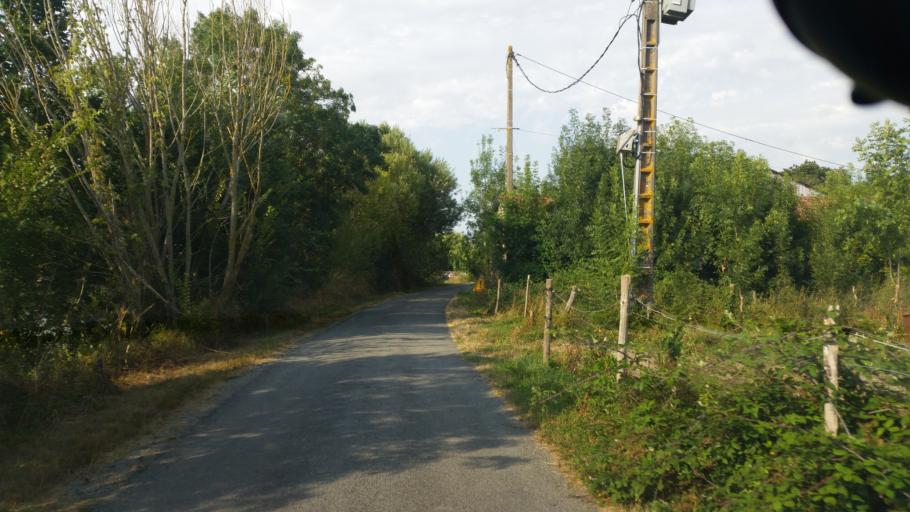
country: FR
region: Pays de la Loire
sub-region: Departement de la Vendee
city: Vix
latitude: 46.3260
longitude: -0.8682
